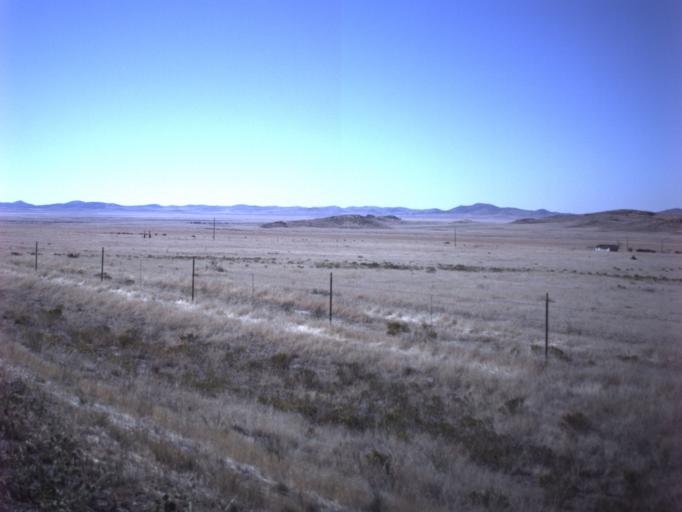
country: US
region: Utah
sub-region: Tooele County
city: Grantsville
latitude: 40.4006
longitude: -112.7479
